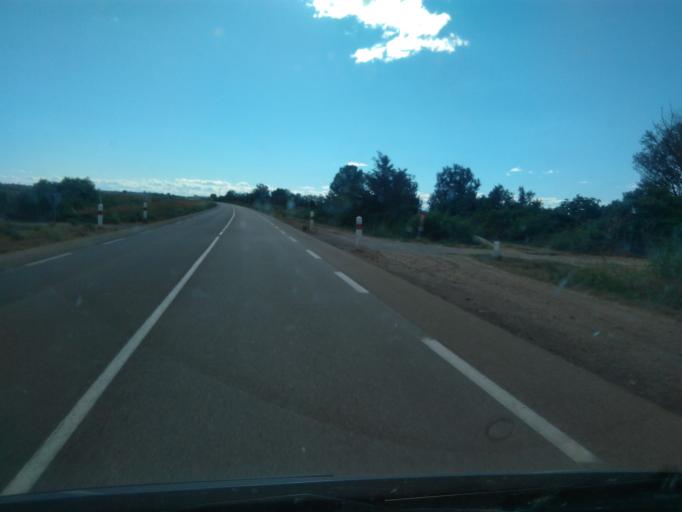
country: FR
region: Languedoc-Roussillon
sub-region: Departement du Gard
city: Fourques
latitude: 43.6829
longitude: 4.5386
